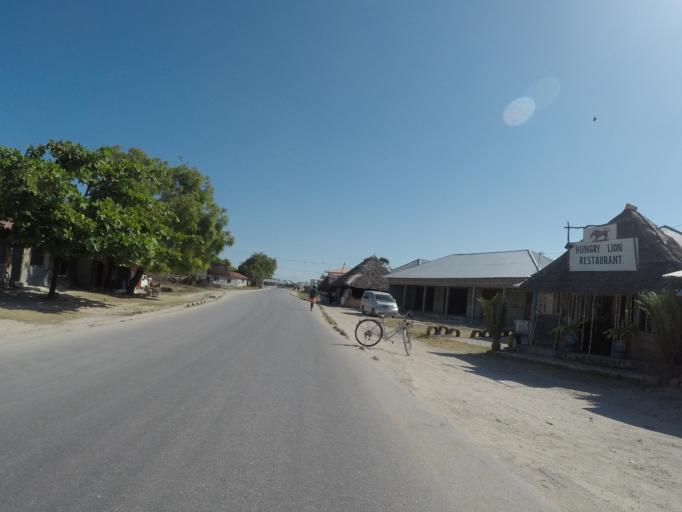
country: TZ
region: Zanzibar Central/South
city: Nganane
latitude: -6.2655
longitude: 39.5320
